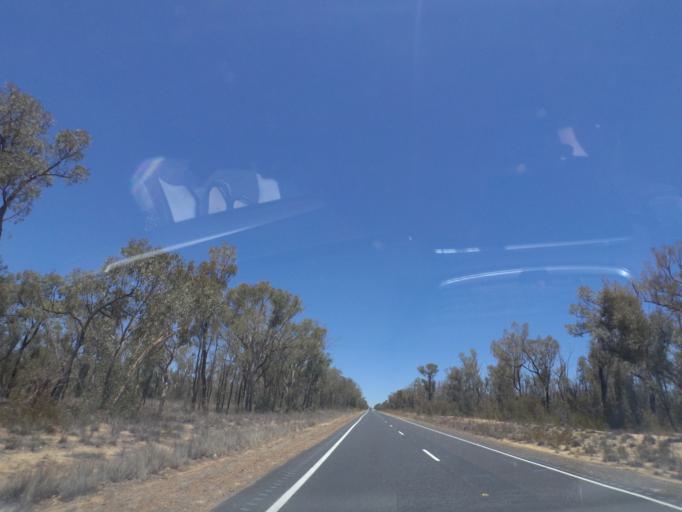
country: AU
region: New South Wales
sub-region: Warrumbungle Shire
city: Coonabarabran
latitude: -30.9493
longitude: 149.4216
